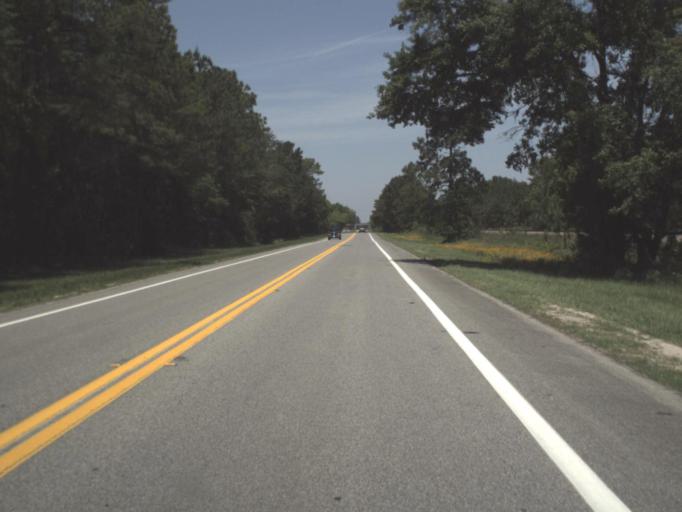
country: US
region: Florida
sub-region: Suwannee County
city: Live Oak
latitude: 30.3378
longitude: -83.0775
